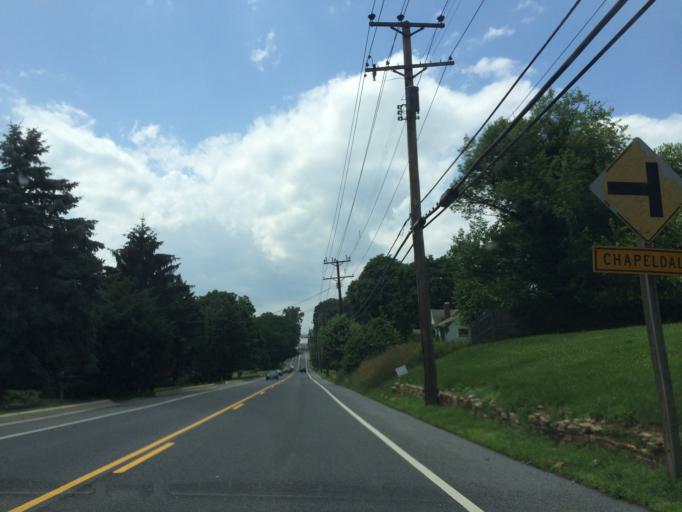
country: US
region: Maryland
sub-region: Baltimore County
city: Randallstown
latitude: 39.3949
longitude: -76.8549
